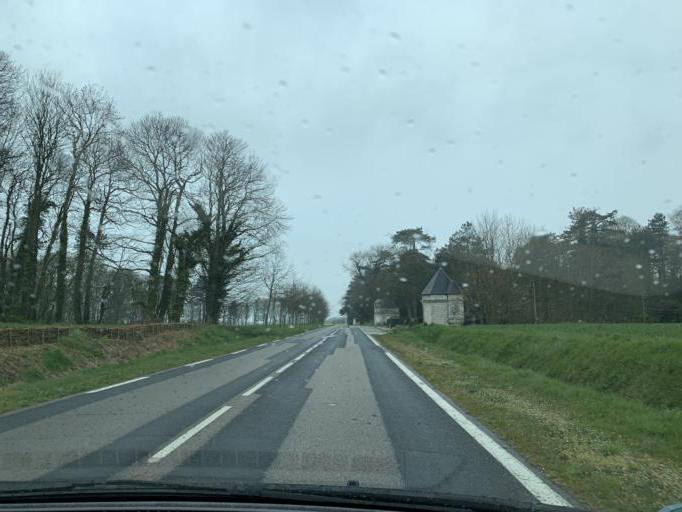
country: FR
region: Haute-Normandie
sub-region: Departement de la Seine-Maritime
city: Etretat
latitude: 49.6914
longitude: 0.2054
